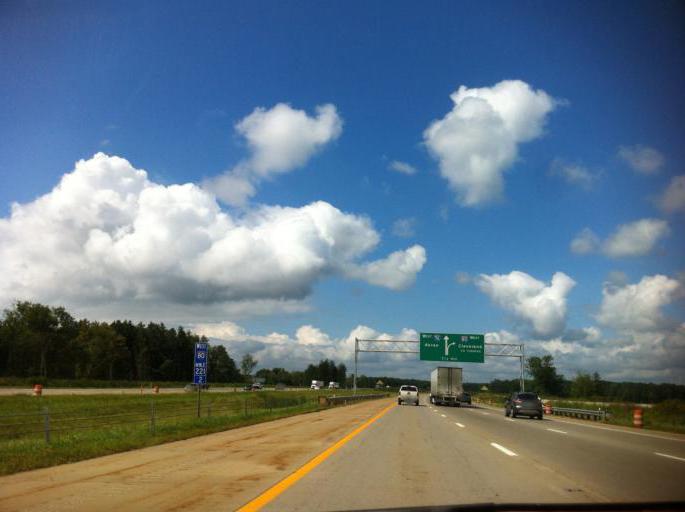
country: US
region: Ohio
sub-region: Trumbull County
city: Mineral Ridge
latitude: 41.1185
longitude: -80.7980
